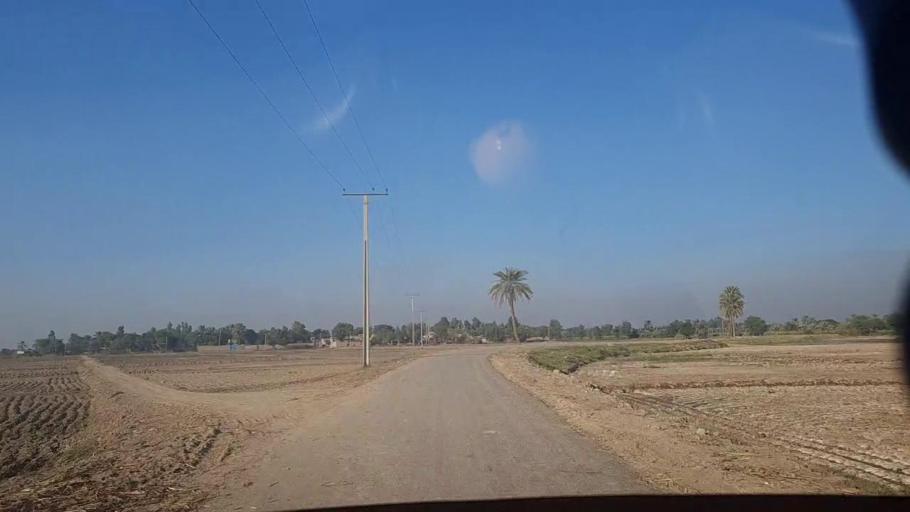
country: PK
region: Sindh
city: Sobhadero
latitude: 27.3845
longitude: 68.4171
